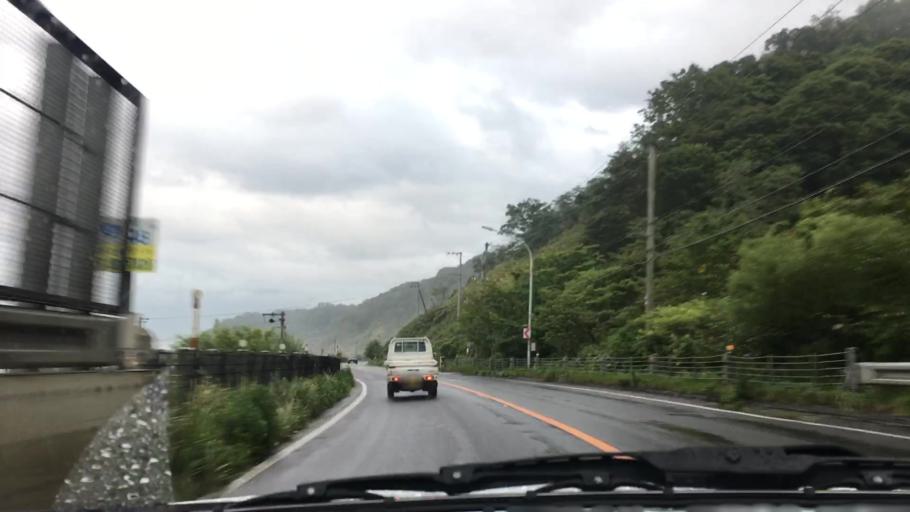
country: JP
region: Hokkaido
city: Nanae
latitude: 42.1277
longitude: 140.5158
